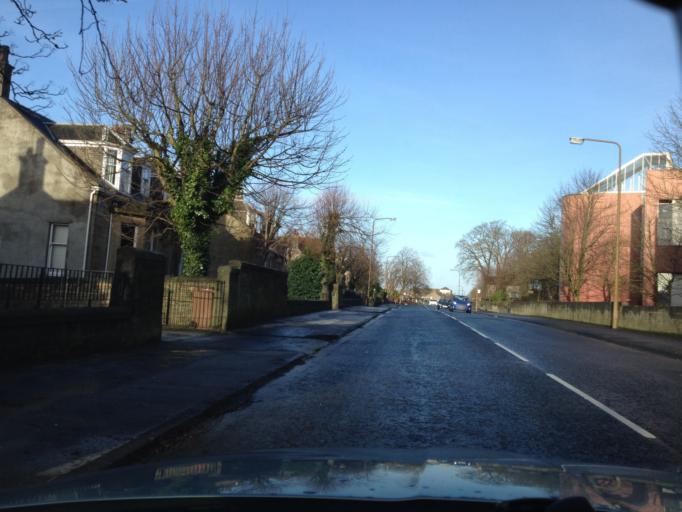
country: GB
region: Scotland
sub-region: West Lothian
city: Bathgate
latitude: 55.8985
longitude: -3.6329
